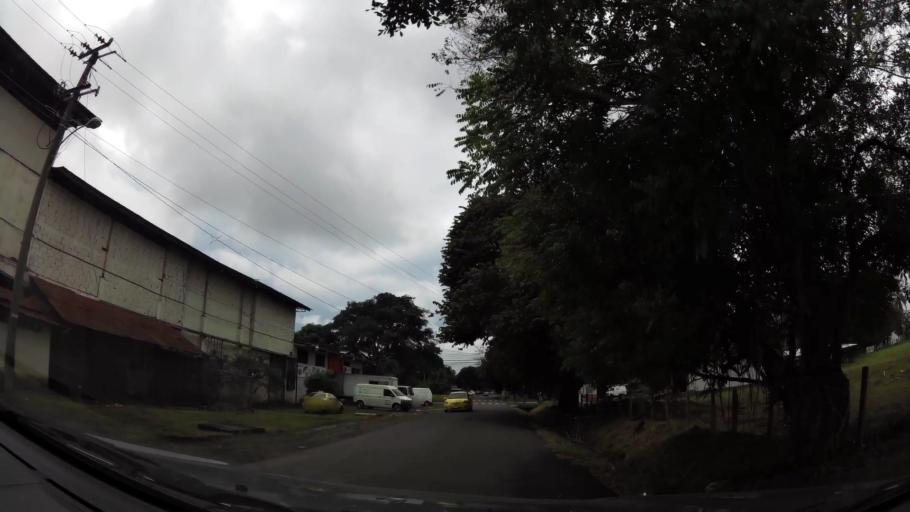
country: PA
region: Chiriqui
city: David
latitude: 8.4262
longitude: -82.4326
